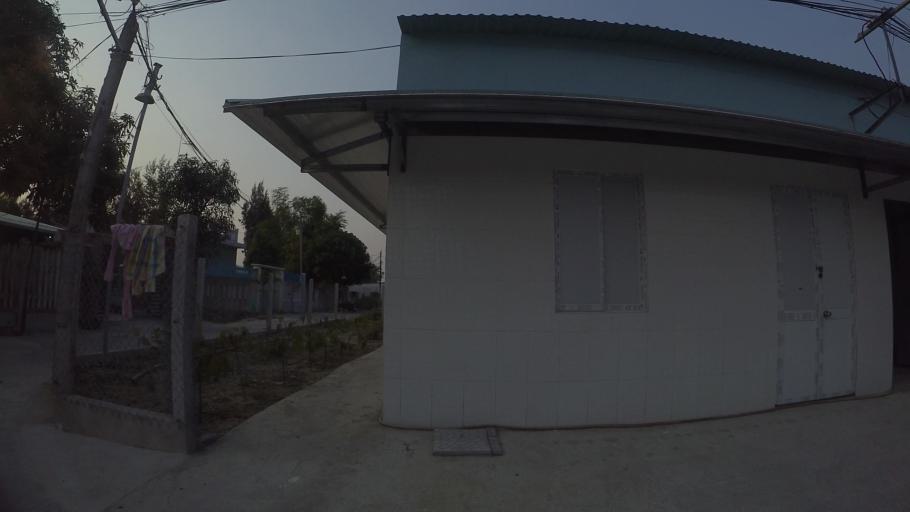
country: VN
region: Da Nang
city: Ngu Hanh Son
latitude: 15.9524
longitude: 108.2532
